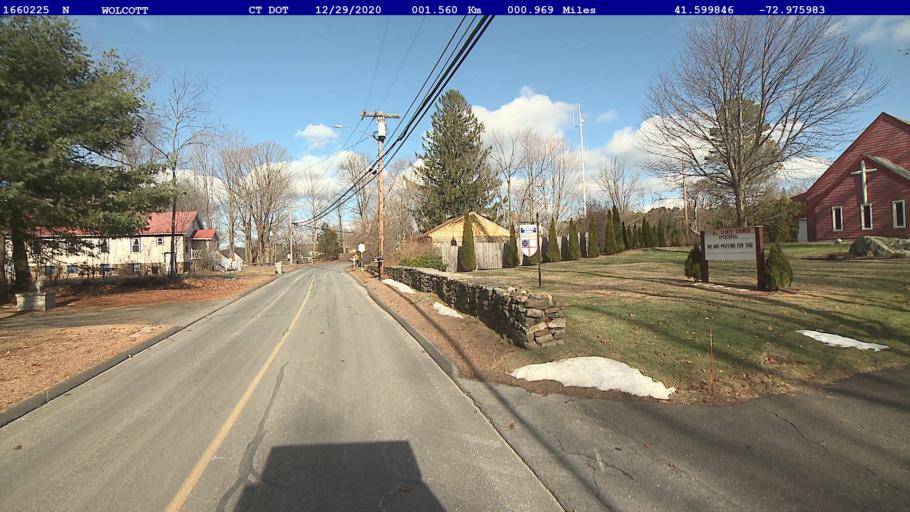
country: US
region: Connecticut
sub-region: New Haven County
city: Wolcott
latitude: 41.5999
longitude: -72.9760
